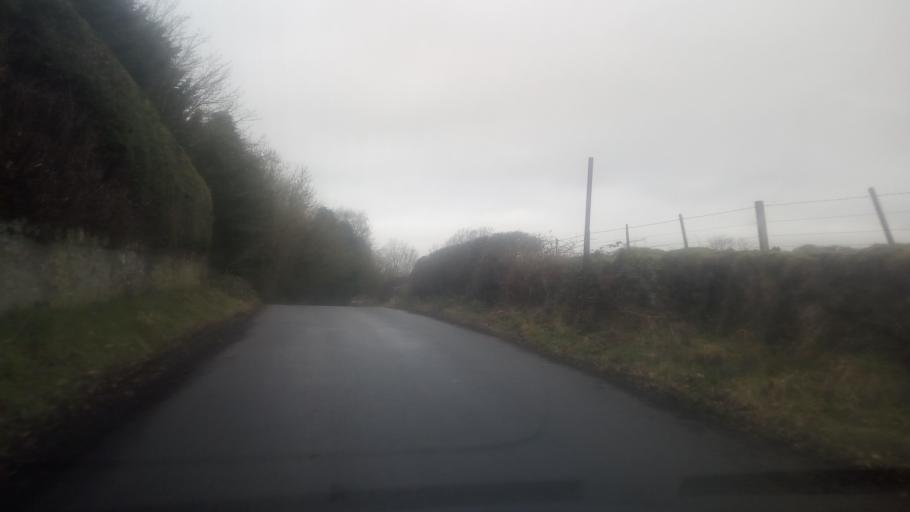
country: GB
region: Scotland
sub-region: The Scottish Borders
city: Kelso
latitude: 55.5679
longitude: -2.4808
